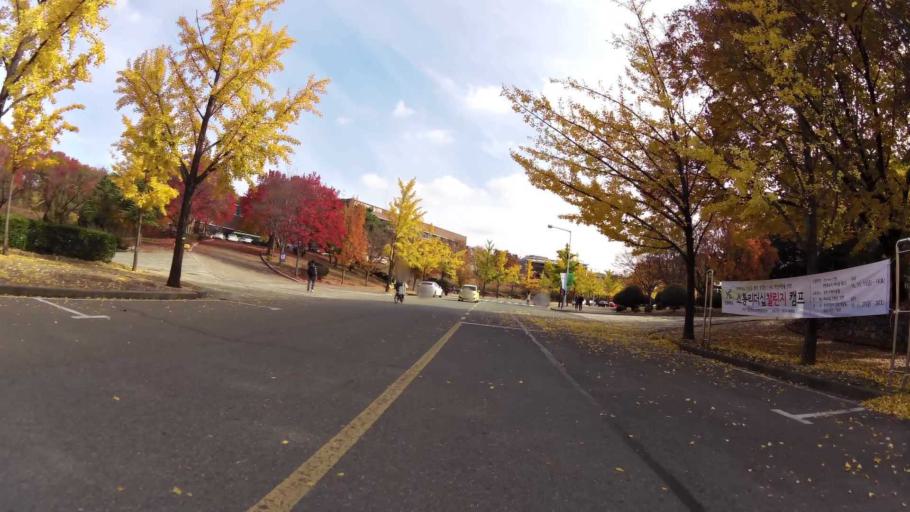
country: KR
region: Gyeongsangbuk-do
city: Gyeongsan-si
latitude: 35.8348
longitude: 128.7561
